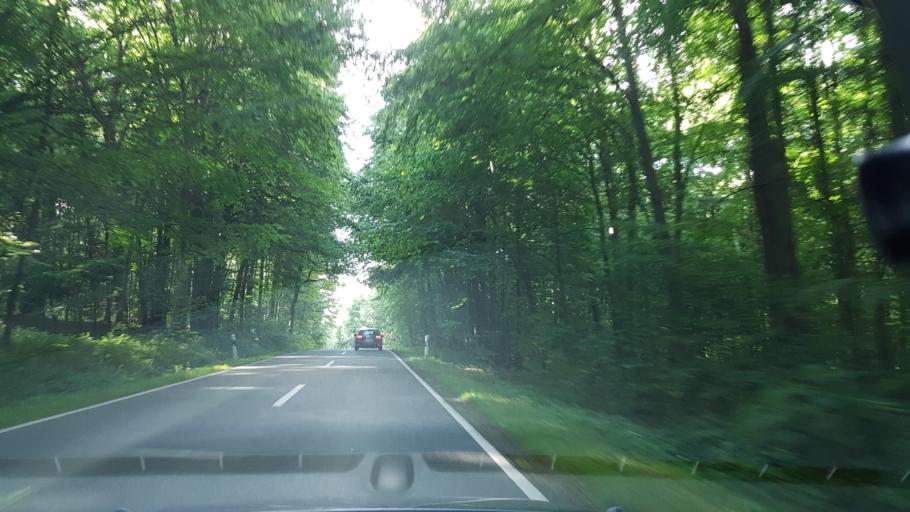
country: DE
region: Lower Saxony
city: Elze
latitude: 52.1281
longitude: 9.6749
